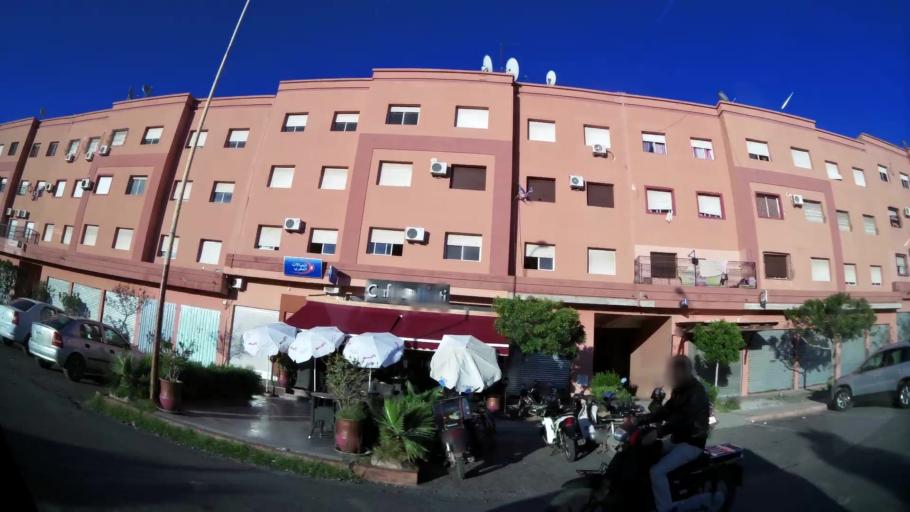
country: MA
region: Marrakech-Tensift-Al Haouz
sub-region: Marrakech
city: Marrakesh
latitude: 31.7483
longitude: -8.1132
